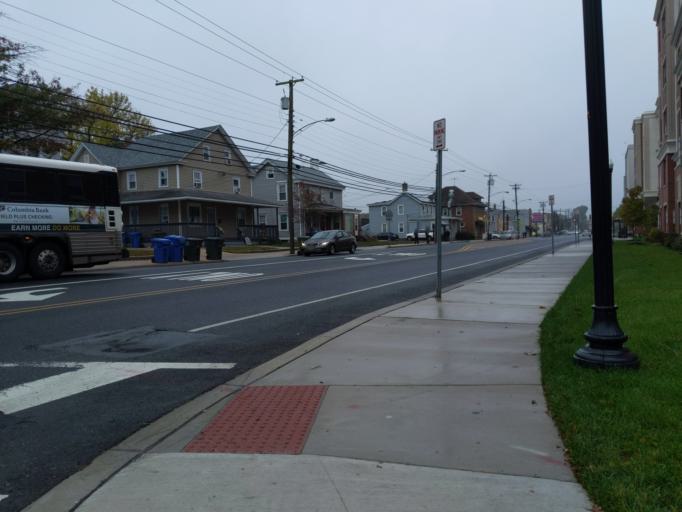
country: US
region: New Jersey
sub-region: Gloucester County
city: Glassboro
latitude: 39.7049
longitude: -75.1116
